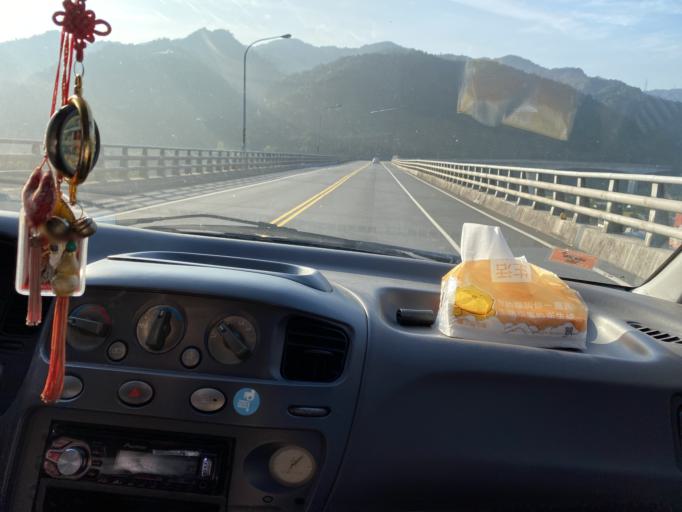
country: TW
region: Taiwan
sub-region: Keelung
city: Keelung
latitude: 25.0468
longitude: 121.7784
